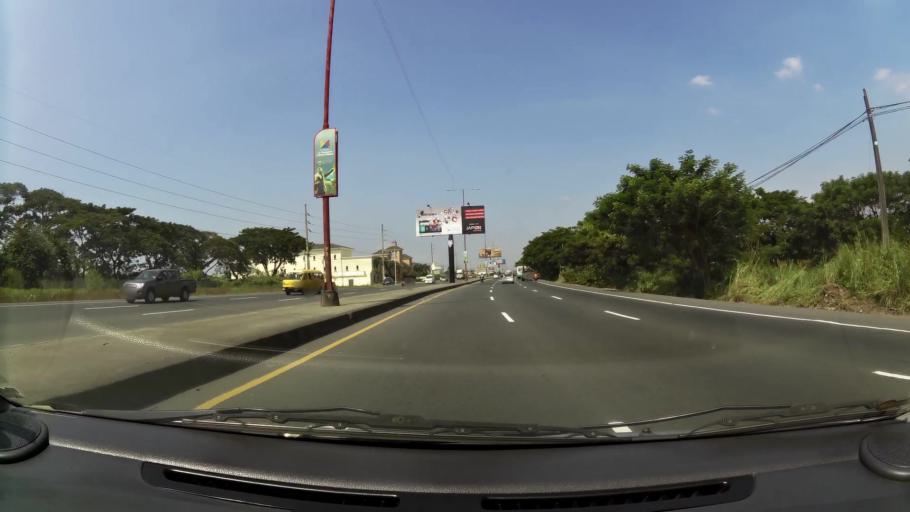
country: EC
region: Guayas
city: Eloy Alfaro
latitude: -2.0511
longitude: -79.8848
